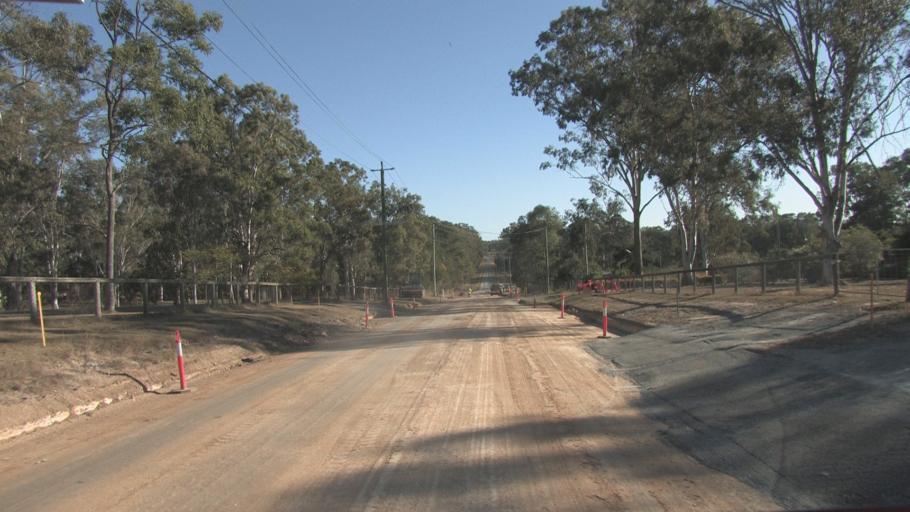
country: AU
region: Queensland
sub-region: Logan
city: Cedar Vale
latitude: -27.8327
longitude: 153.0029
